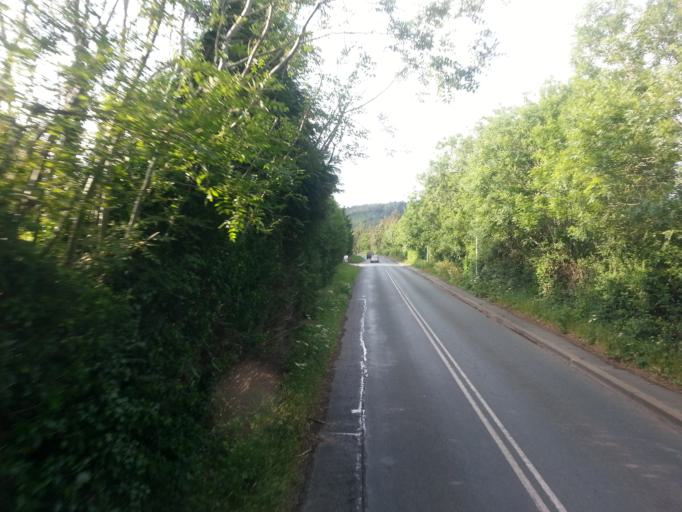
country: IE
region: Leinster
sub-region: Wicklow
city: Enniskerry
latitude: 53.2074
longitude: -6.1741
